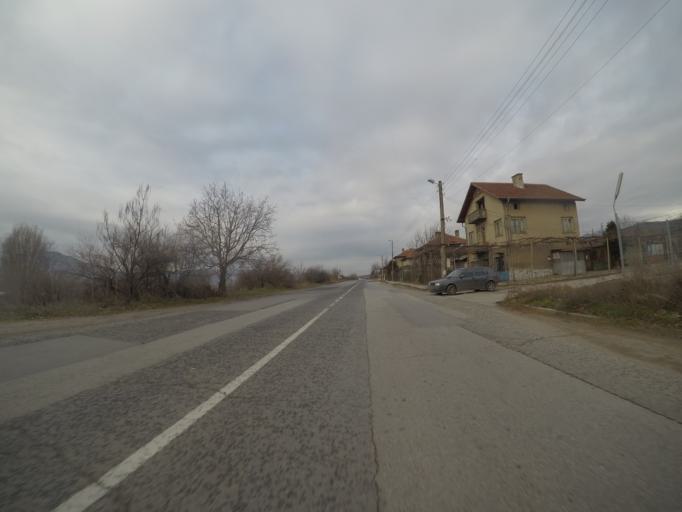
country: BG
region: Kyustendil
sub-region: Obshtina Kocherinovo
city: Kocherinovo
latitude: 42.1186
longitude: 23.0386
